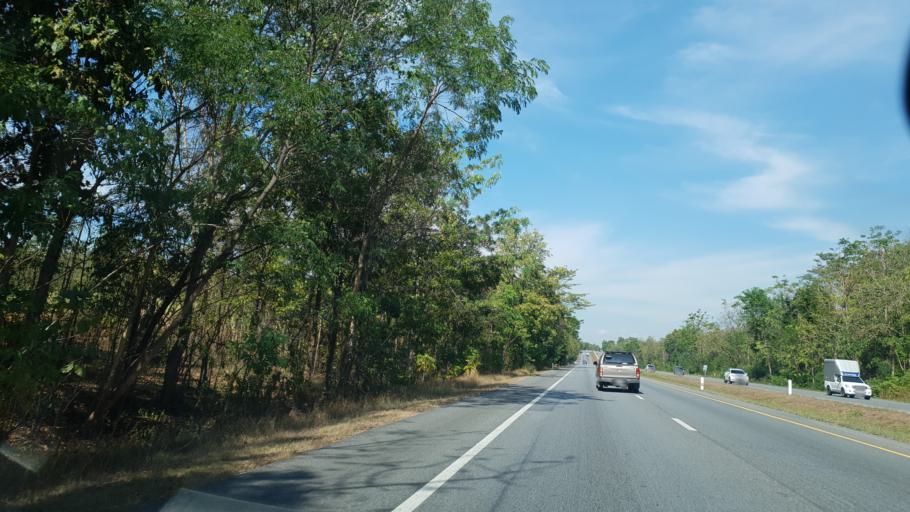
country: TH
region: Uttaradit
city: Thong Saen Khan
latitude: 17.4132
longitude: 100.2282
